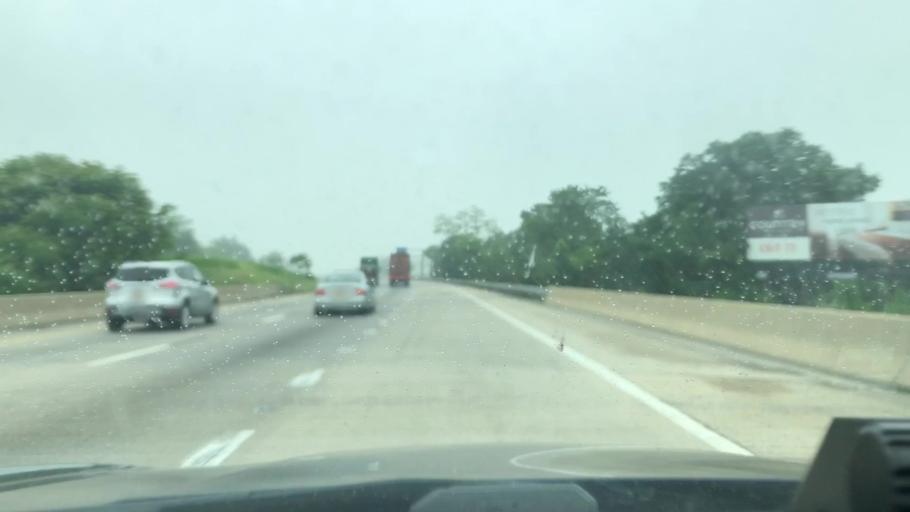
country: US
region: Pennsylvania
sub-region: Dauphin County
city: Skyline View
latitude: 40.3776
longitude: -76.6703
